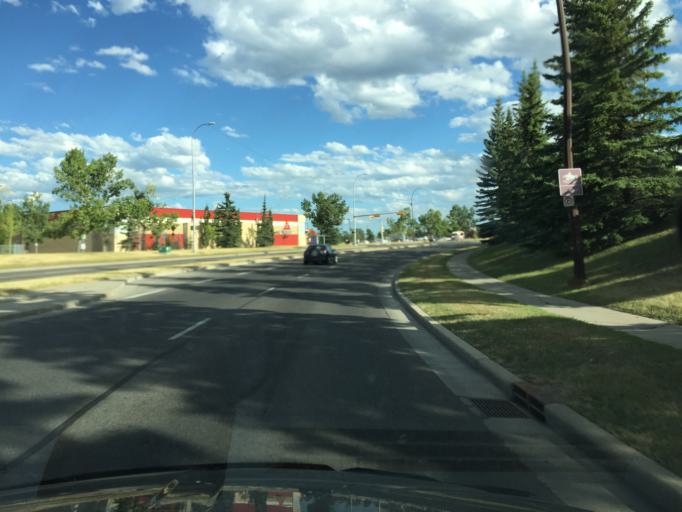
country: CA
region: Alberta
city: Calgary
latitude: 50.9535
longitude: -114.0610
